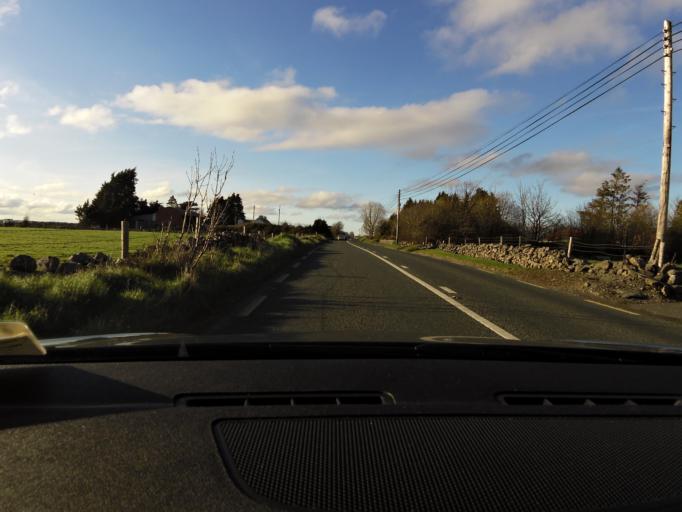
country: IE
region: Connaught
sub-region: Roscommon
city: Roscommon
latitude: 53.6937
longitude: -8.1981
